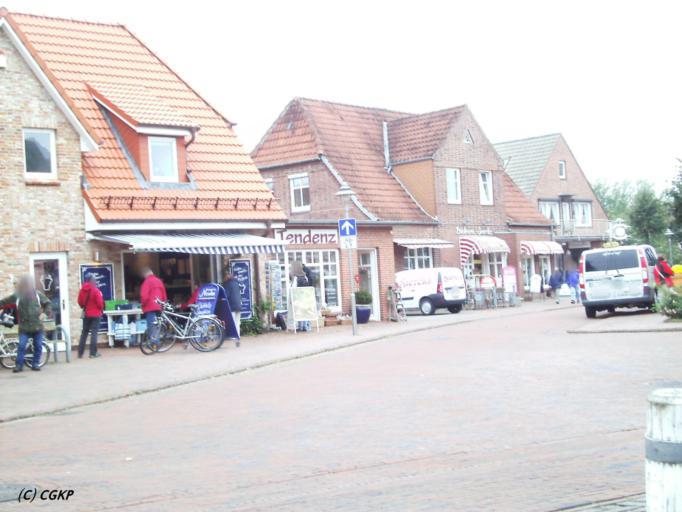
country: DE
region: Schleswig-Holstein
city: Sankt Peter-Ording
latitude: 54.3039
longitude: 8.6379
